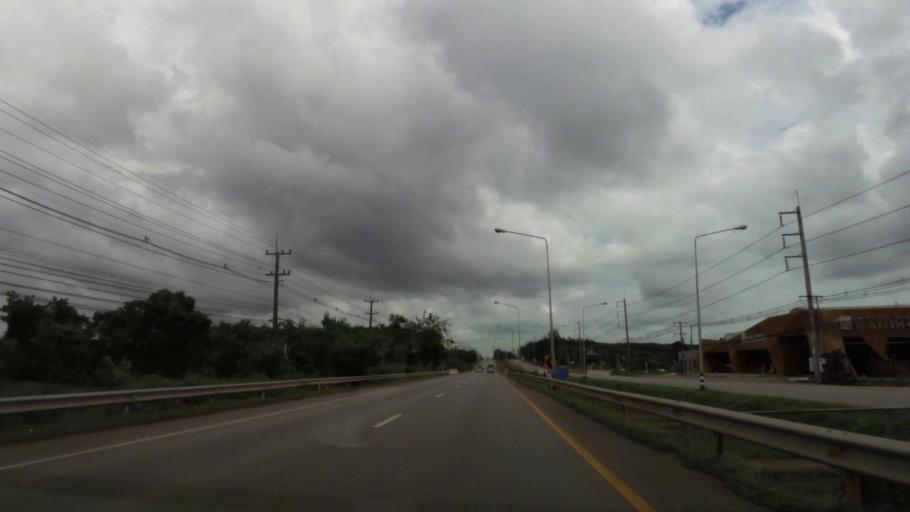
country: TH
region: Chanthaburi
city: Na Yai Am
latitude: 12.7746
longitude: 101.8376
